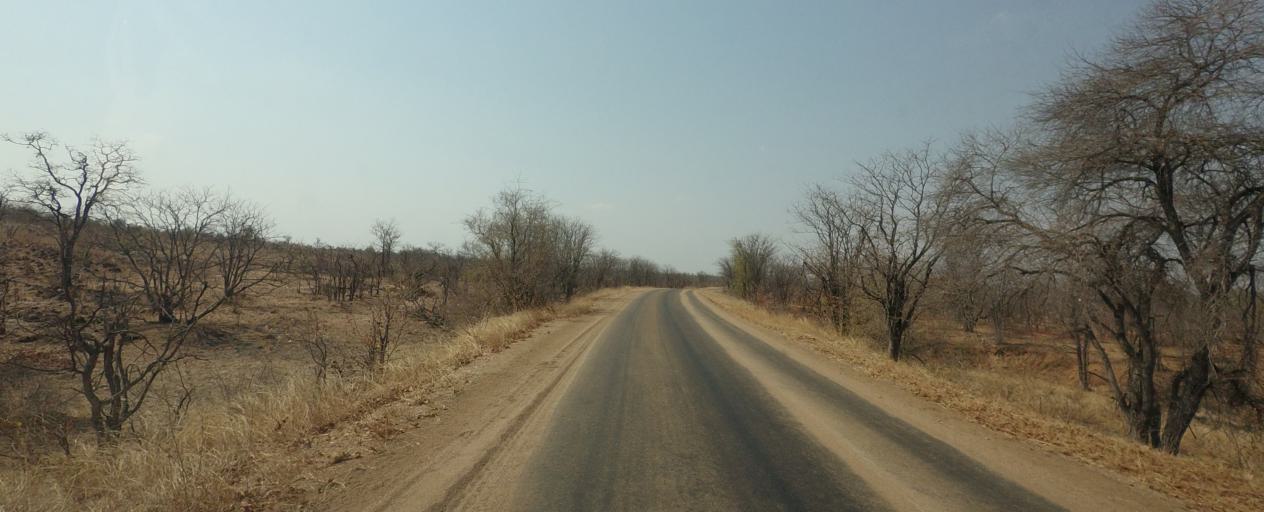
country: ZA
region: Limpopo
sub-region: Mopani District Municipality
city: Giyani
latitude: -23.2014
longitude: 31.3073
